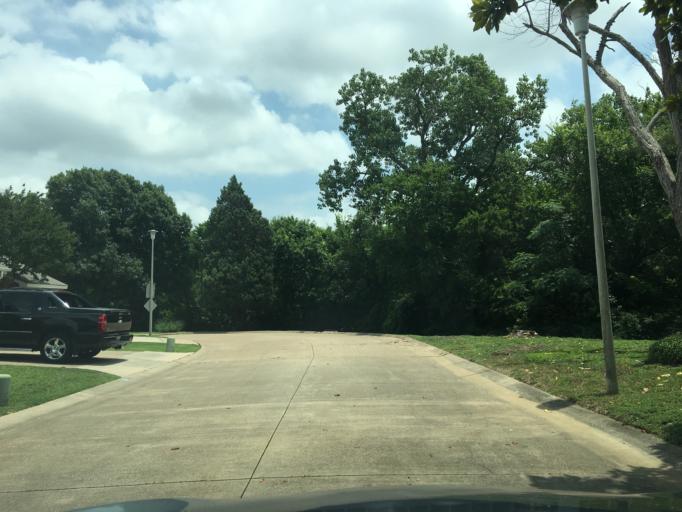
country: US
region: Texas
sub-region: Dallas County
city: Garland
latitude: 32.9307
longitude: -96.6726
